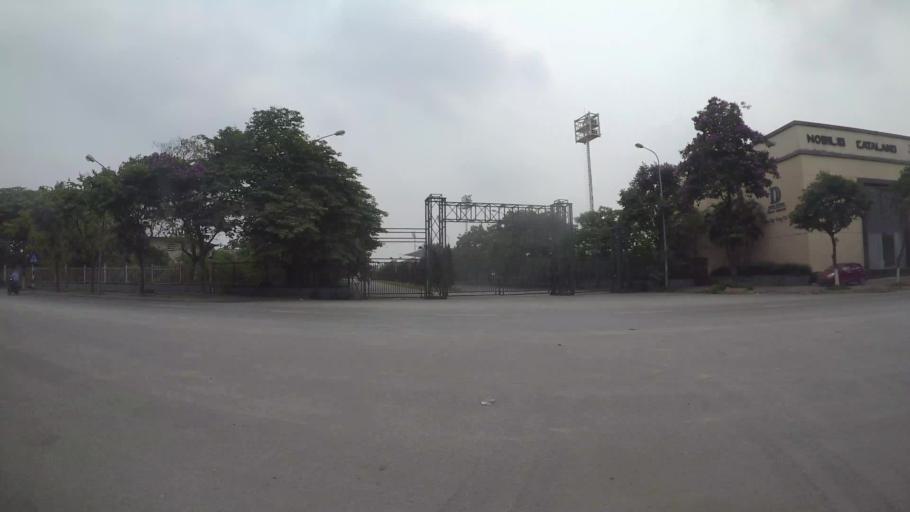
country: VN
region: Ha Noi
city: Cau Dien
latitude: 21.0248
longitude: 105.7639
